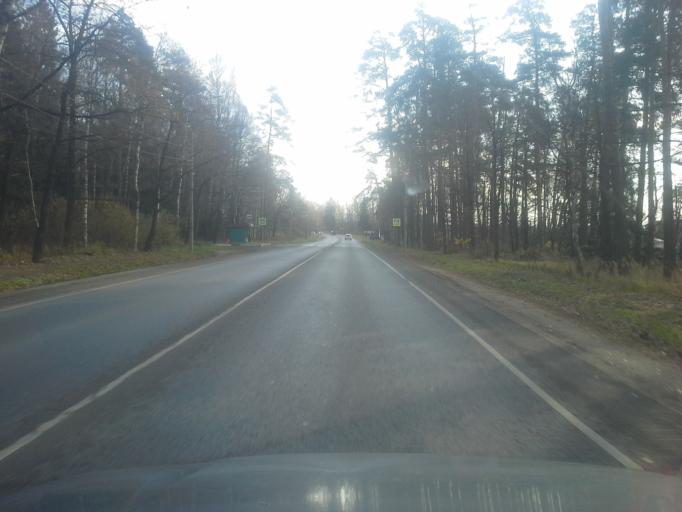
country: RU
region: Moskovskaya
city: Bol'shiye Vyazemy
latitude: 55.6695
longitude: 36.9536
